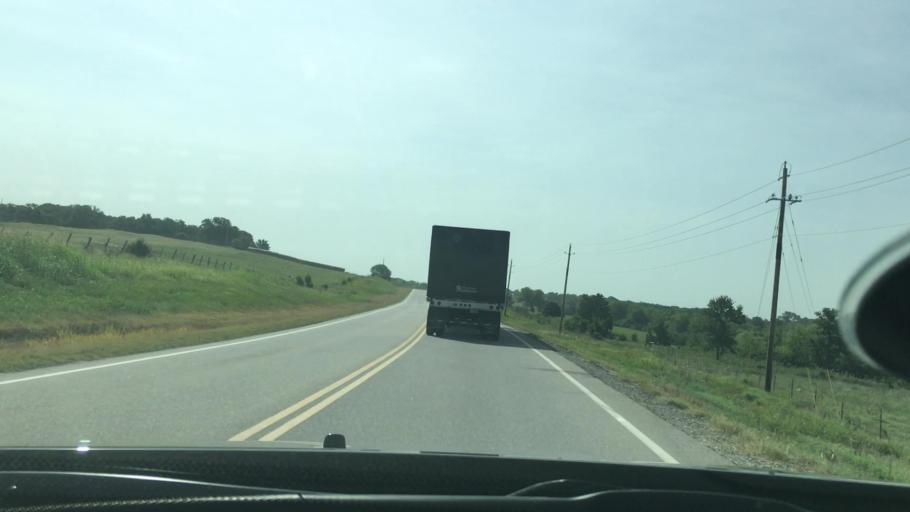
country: US
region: Oklahoma
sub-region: Atoka County
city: Atoka
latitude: 34.4030
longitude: -96.1770
